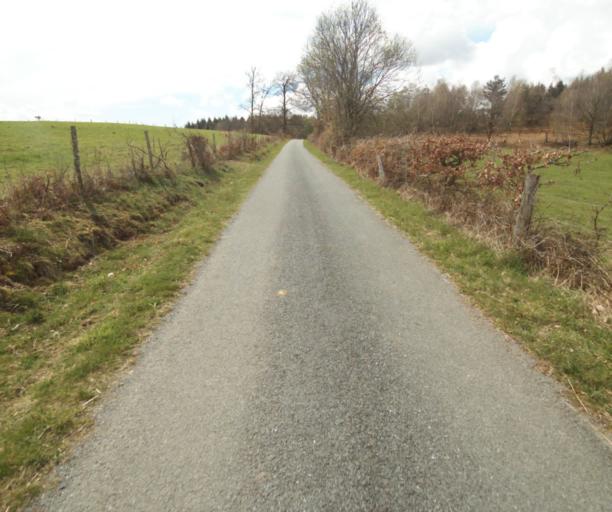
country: FR
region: Limousin
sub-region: Departement de la Correze
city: Correze
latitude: 45.3781
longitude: 1.9641
